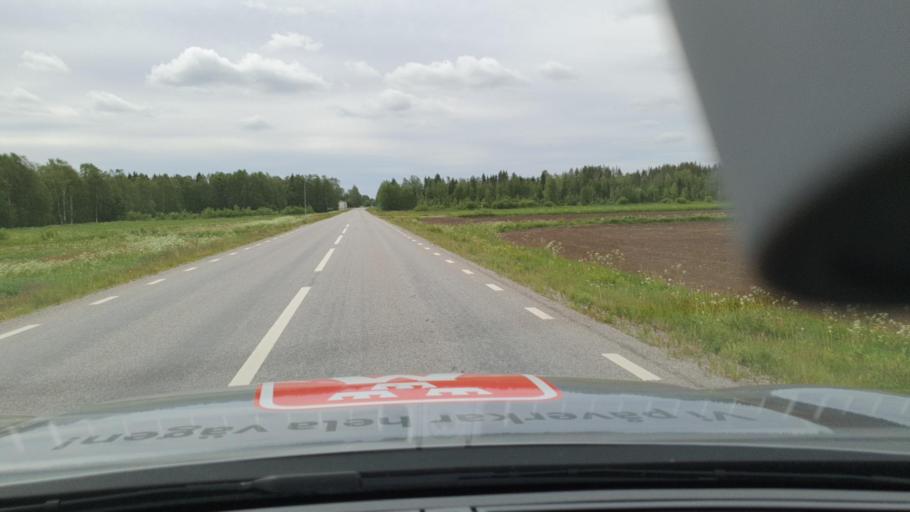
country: SE
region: Norrbotten
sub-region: Kalix Kommun
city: Kalix
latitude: 65.9378
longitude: 23.4603
